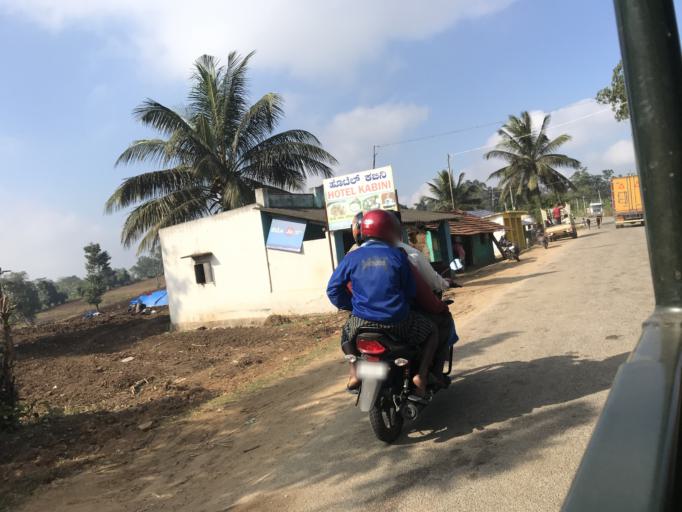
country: IN
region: Karnataka
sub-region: Mysore
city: Heggadadevankote
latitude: 11.9452
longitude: 76.2395
